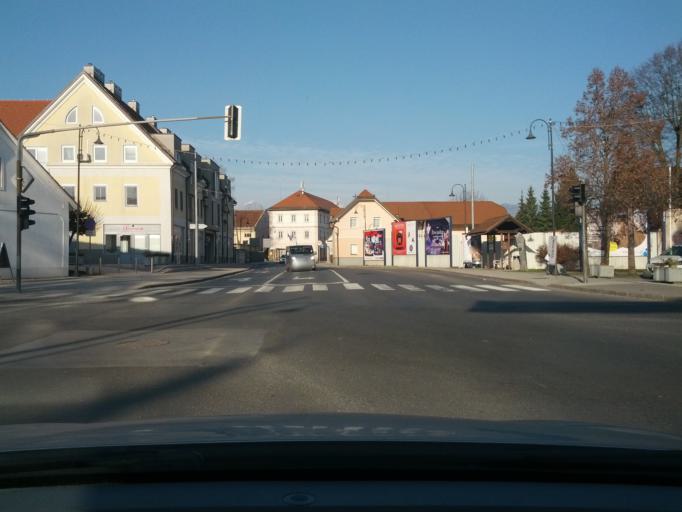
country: SI
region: Menges
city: Menges
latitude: 46.1637
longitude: 14.5712
